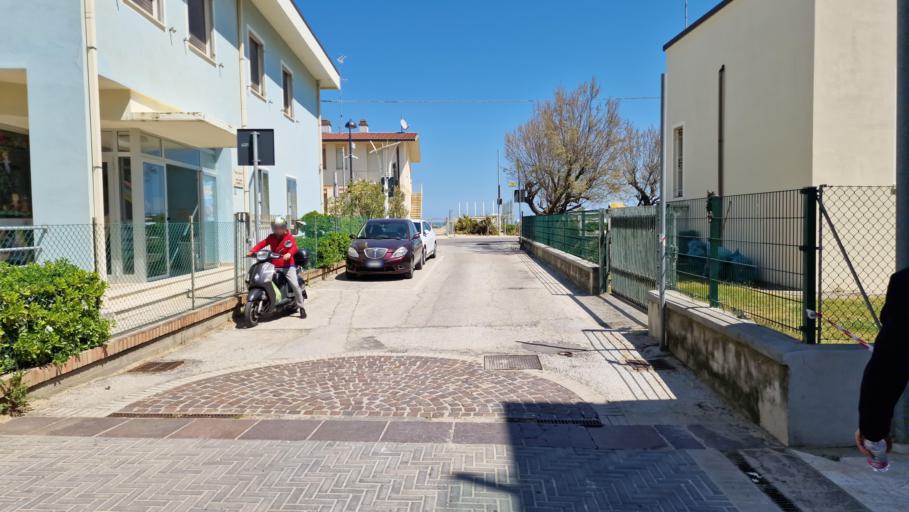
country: IT
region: Emilia-Romagna
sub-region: Provincia di Rimini
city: Bellaria-Igea Marina
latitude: 44.1359
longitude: 12.4803
